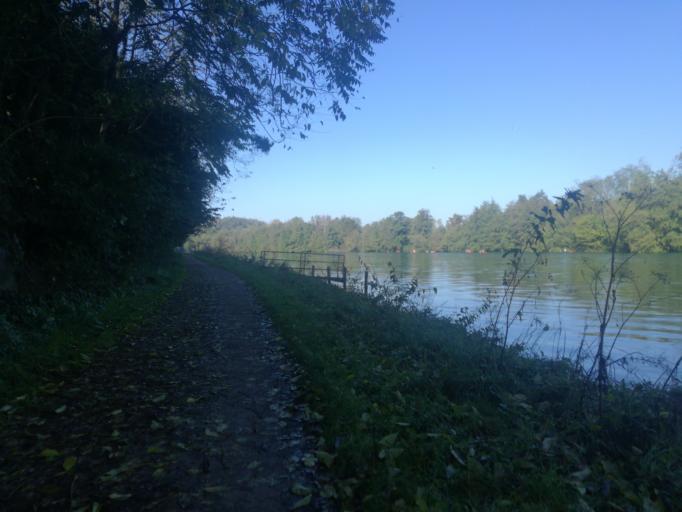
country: IT
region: Lombardy
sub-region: Provincia di Bergamo
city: Bottanuco
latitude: 45.6271
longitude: 9.5057
